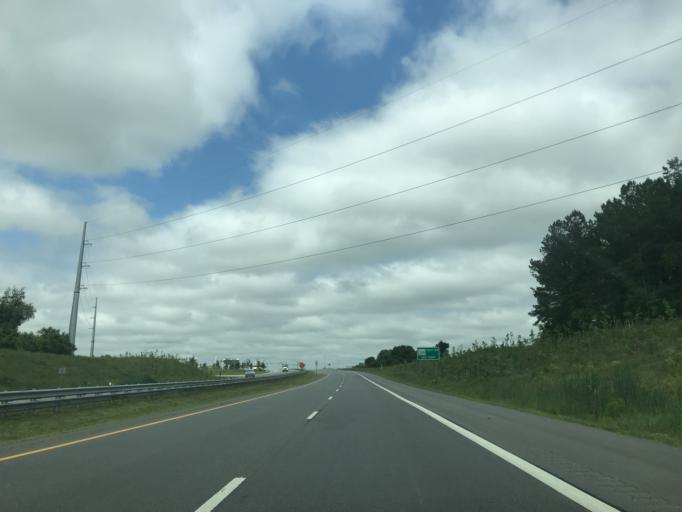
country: US
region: Maryland
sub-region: Caroline County
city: Ridgely
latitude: 38.9232
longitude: -75.9522
